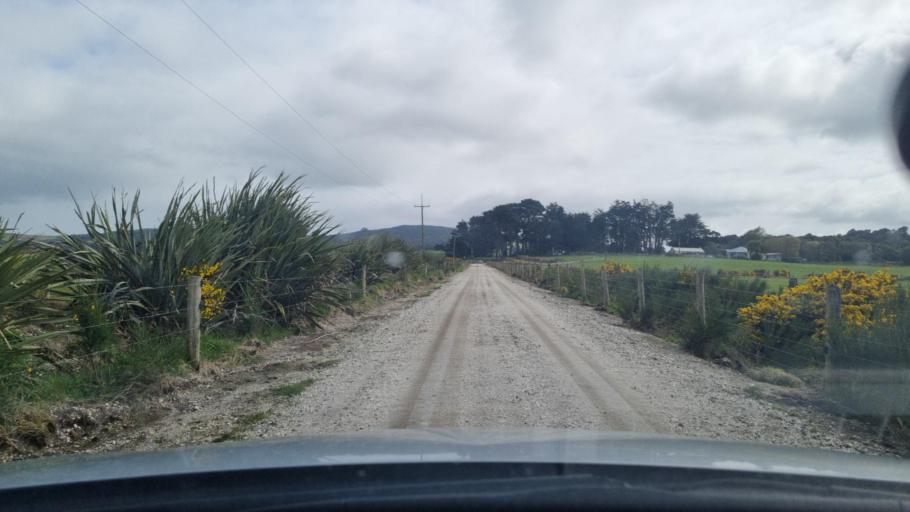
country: NZ
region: Southland
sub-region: Invercargill City
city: Bluff
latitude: -46.5258
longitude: 168.3019
